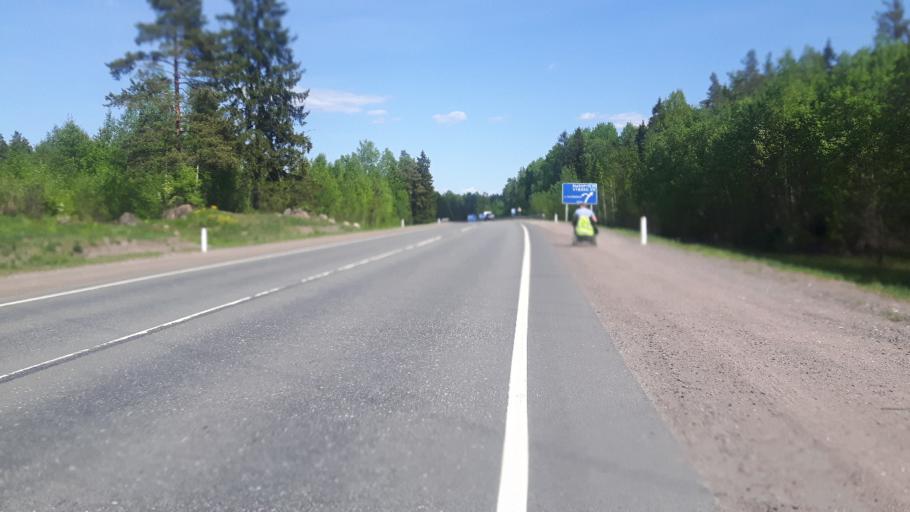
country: RU
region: Leningrad
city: Vyborg
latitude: 60.7441
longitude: 28.6619
